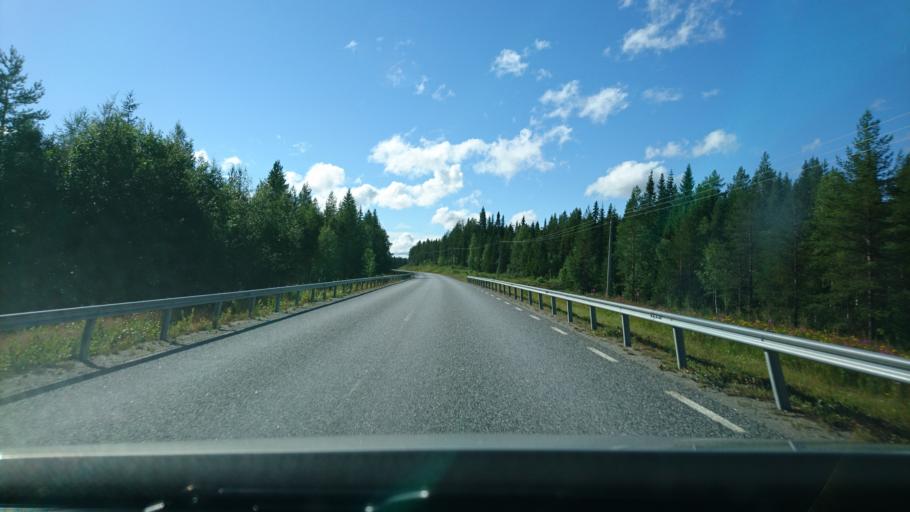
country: SE
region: Vaesterbotten
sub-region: Vilhelmina Kommun
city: Vilhelmina
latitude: 64.3658
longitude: 16.9441
